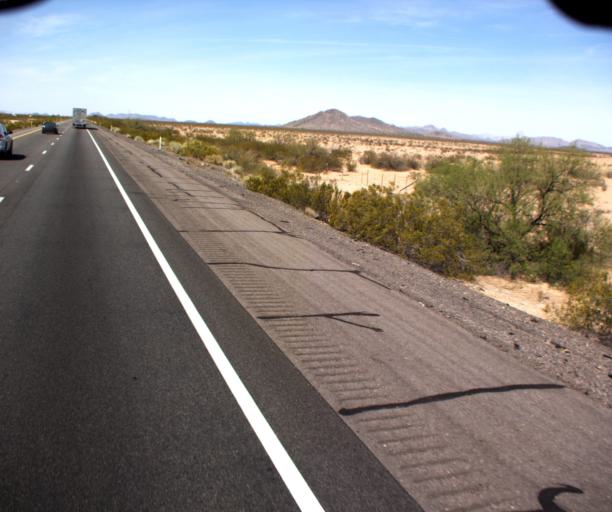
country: US
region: Arizona
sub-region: La Paz County
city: Salome
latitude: 33.5796
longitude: -113.4211
